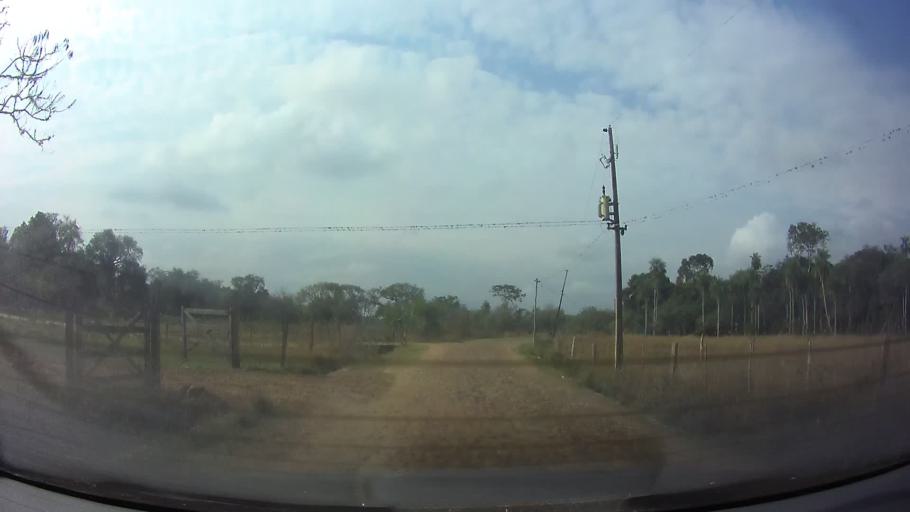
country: PY
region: Cordillera
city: Arroyos y Esteros
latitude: -25.0035
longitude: -57.1985
